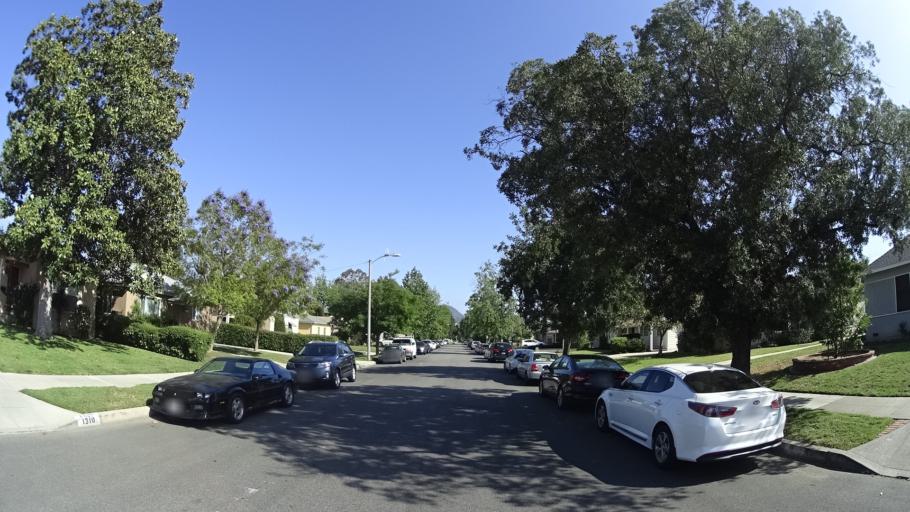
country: US
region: California
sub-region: Los Angeles County
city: North Hollywood
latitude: 34.1728
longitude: -118.3516
